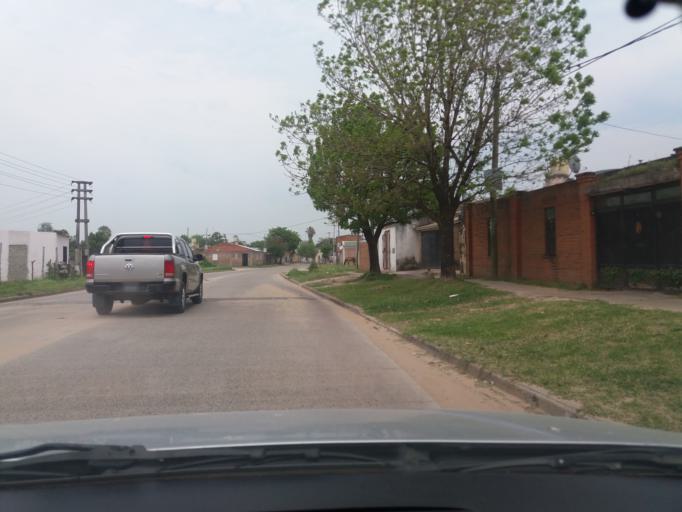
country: AR
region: Corrientes
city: Corrientes
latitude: -27.5104
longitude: -58.7987
